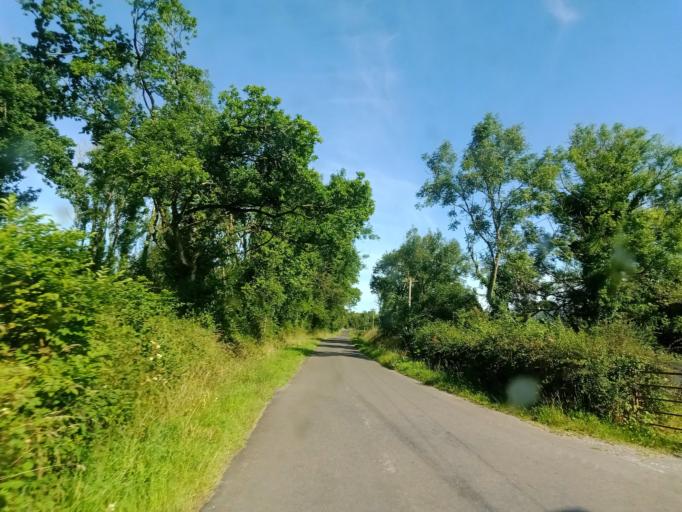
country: IE
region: Leinster
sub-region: Kilkenny
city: Ballyragget
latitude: 52.7719
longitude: -7.4119
